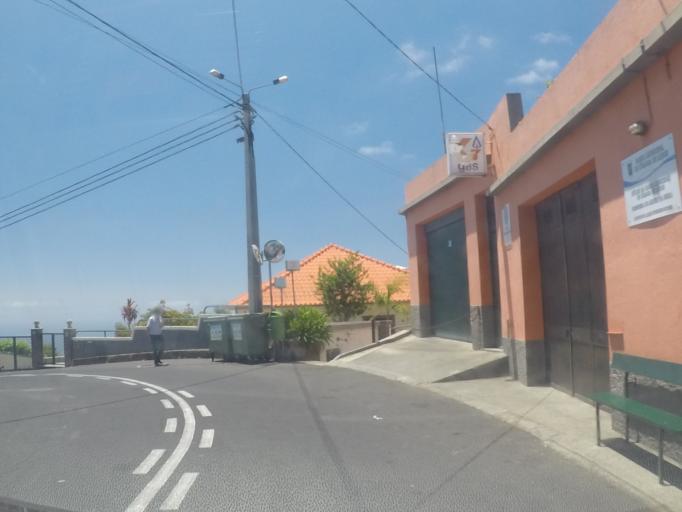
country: PT
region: Madeira
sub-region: Camara de Lobos
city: Curral das Freiras
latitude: 32.6809
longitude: -16.9909
